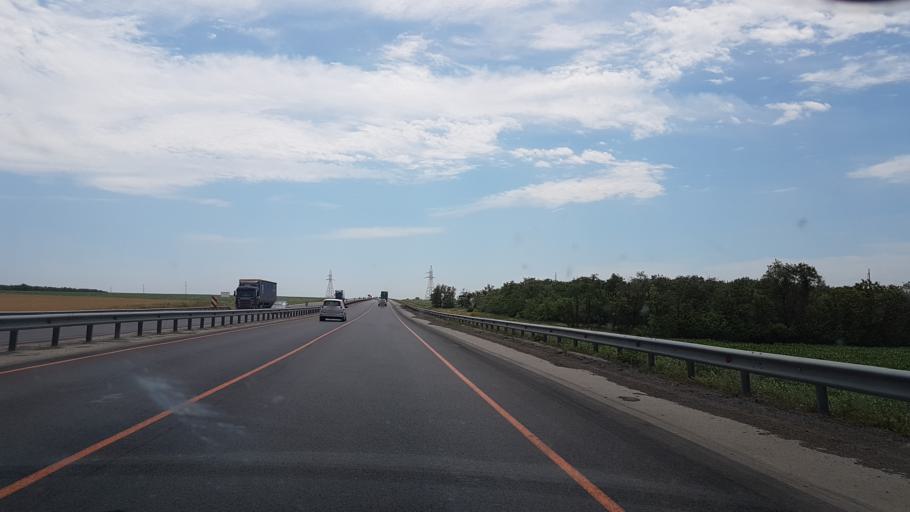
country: RU
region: Rostov
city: Zverevo
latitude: 47.9663
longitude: 40.2175
